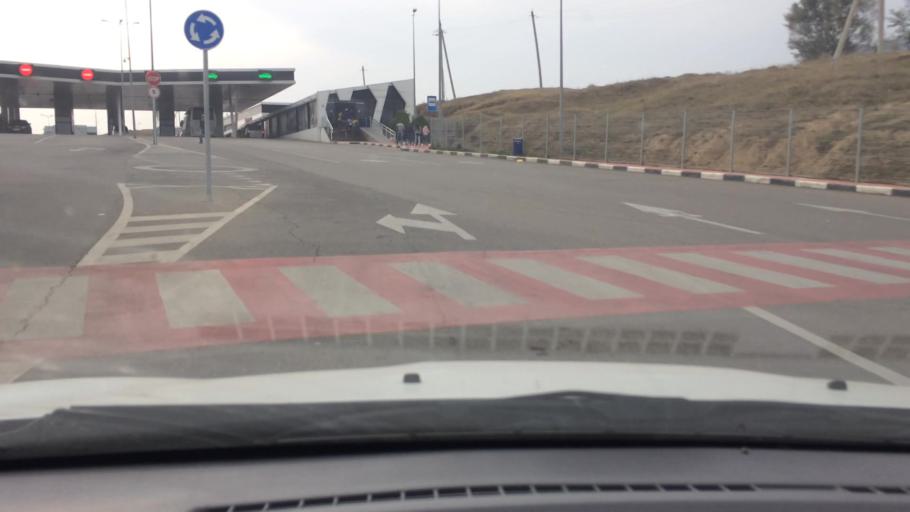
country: AM
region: Tavush
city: Bagratashen
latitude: 41.2279
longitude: 44.8296
